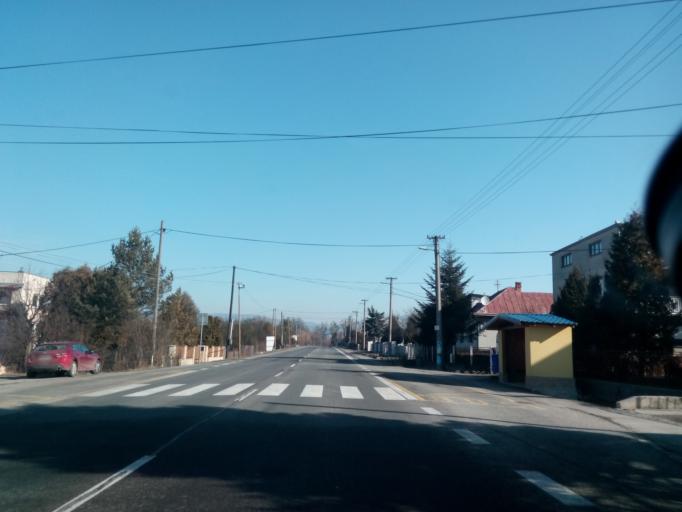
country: SK
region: Kosicky
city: Secovce
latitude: 48.7353
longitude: 21.4673
